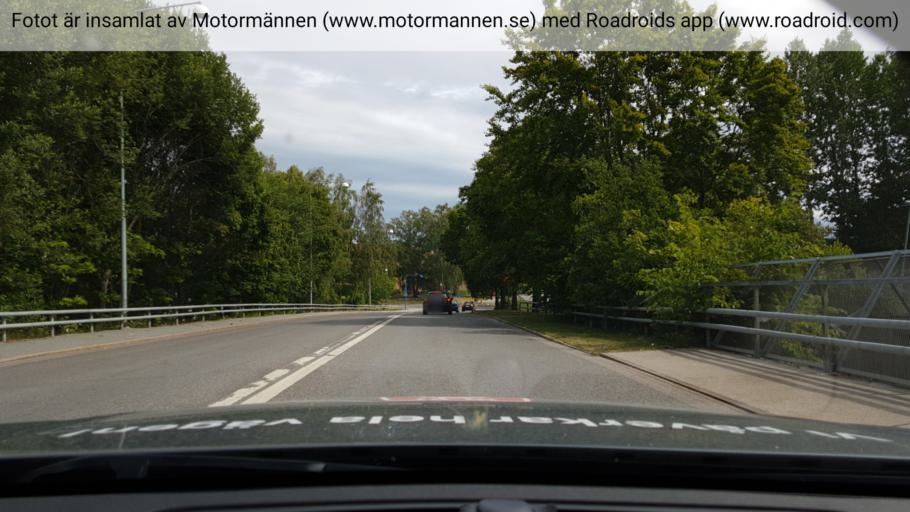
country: SE
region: Stockholm
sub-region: Nynashamns Kommun
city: Nynashamn
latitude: 58.9154
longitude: 17.9420
